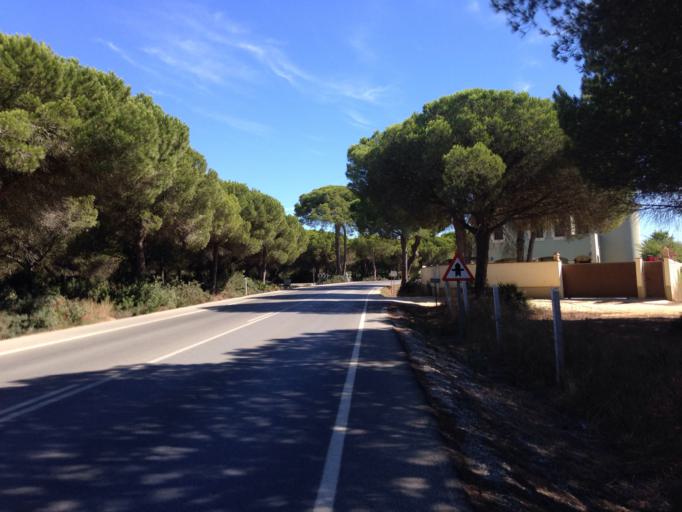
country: ES
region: Andalusia
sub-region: Provincia de Cadiz
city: Conil de la Frontera
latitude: 36.3172
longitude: -6.1047
